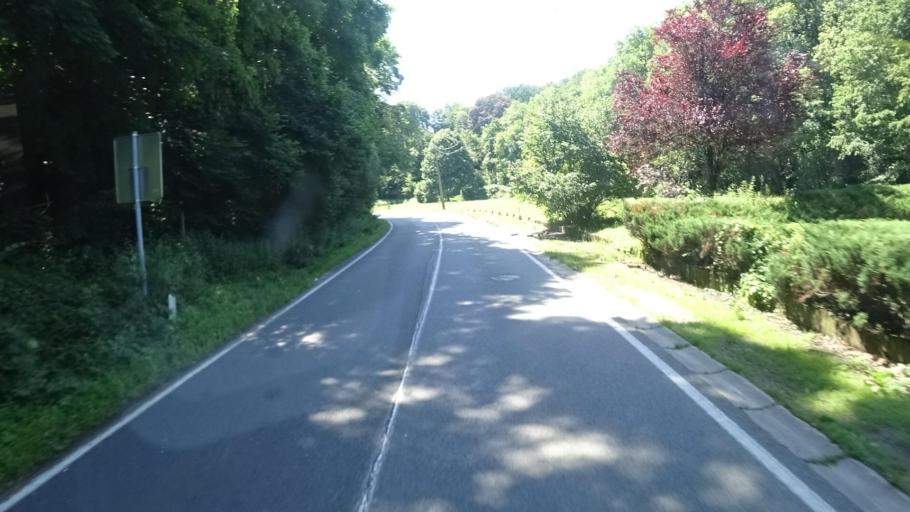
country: BE
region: Wallonia
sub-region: Province de Namur
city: Floreffe
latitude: 50.4238
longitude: 4.7601
